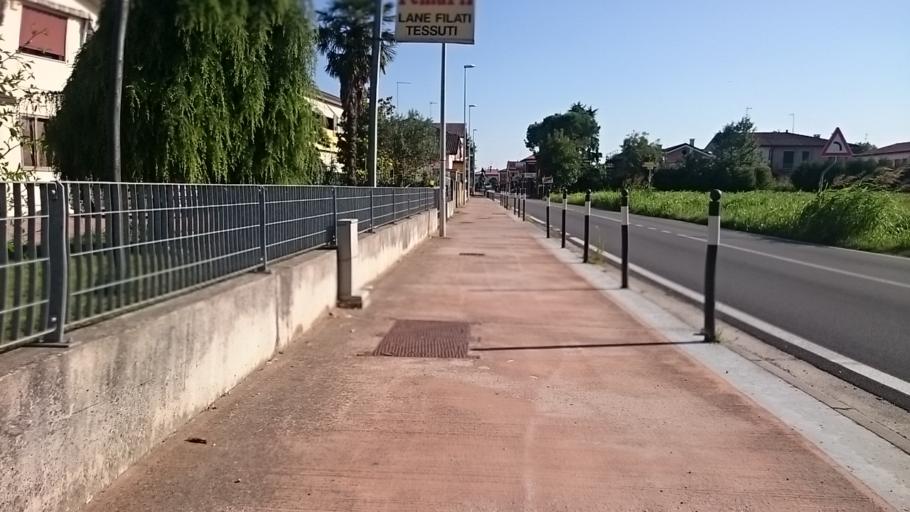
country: IT
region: Veneto
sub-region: Provincia di Padova
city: Villatora
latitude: 45.3710
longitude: 11.9647
